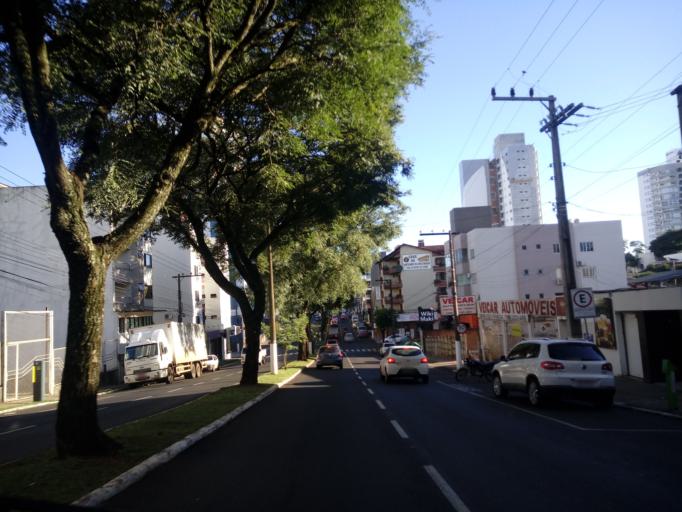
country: BR
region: Santa Catarina
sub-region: Chapeco
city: Chapeco
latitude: -27.0934
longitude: -52.6153
